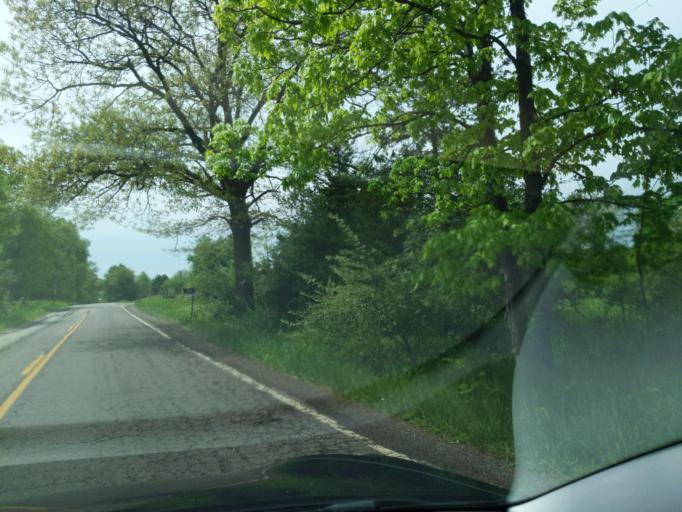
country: US
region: Michigan
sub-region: Ingham County
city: Stockbridge
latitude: 42.4247
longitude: -84.2572
